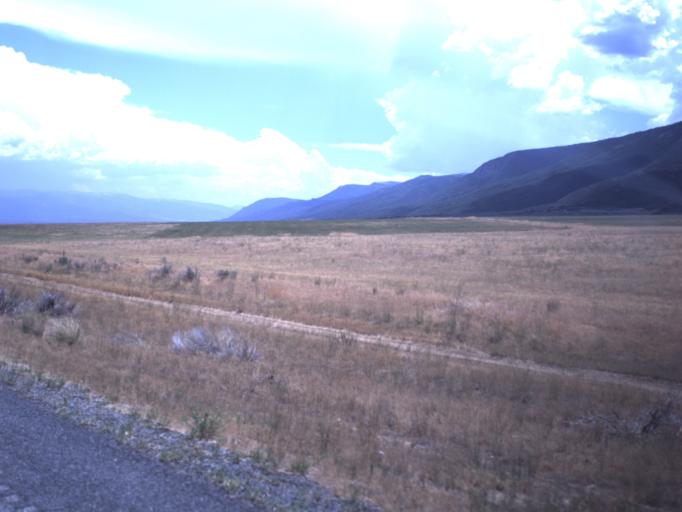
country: US
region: Utah
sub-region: Sanpete County
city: Fountain Green
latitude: 39.6605
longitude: -111.6551
